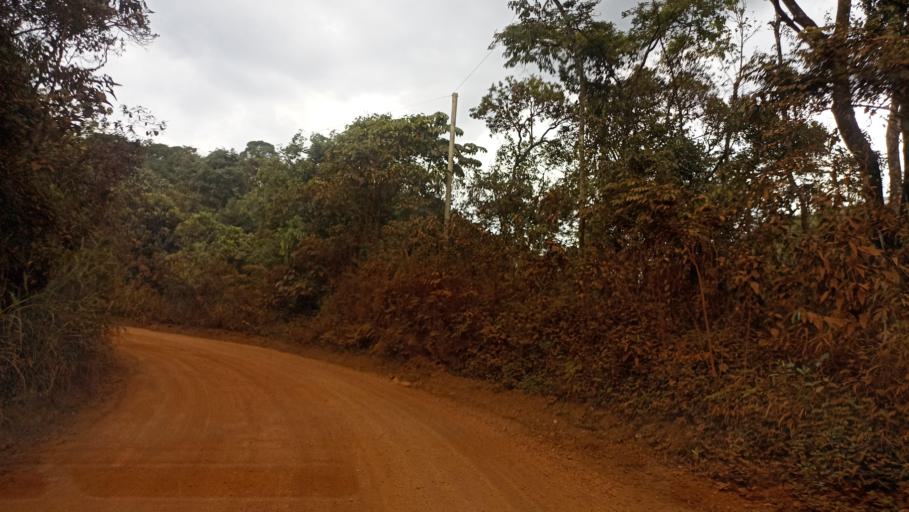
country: BR
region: Minas Gerais
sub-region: Congonhas
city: Congonhas
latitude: -20.4272
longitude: -43.7750
